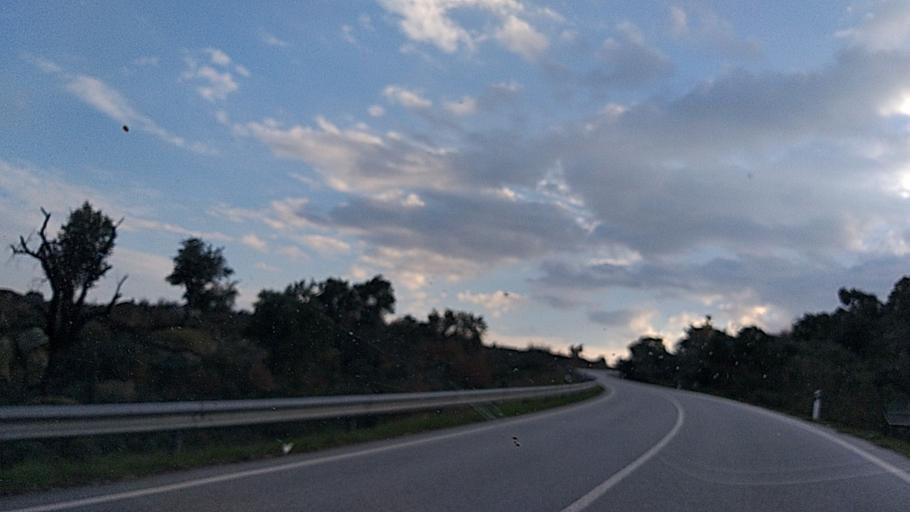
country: ES
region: Castille and Leon
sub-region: Provincia de Salamanca
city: Aldea del Obispo
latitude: 40.6909
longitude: -6.9406
